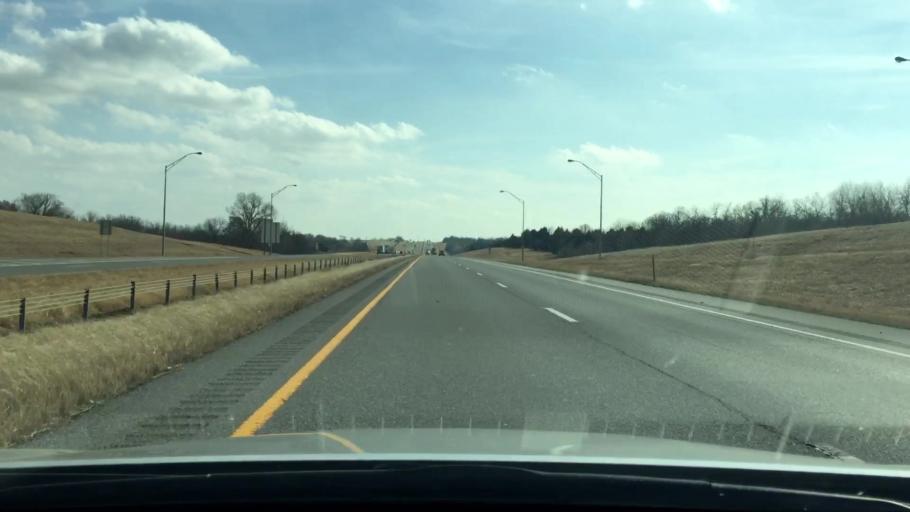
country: US
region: Oklahoma
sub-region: McClain County
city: Purcell
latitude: 34.9804
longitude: -97.3724
